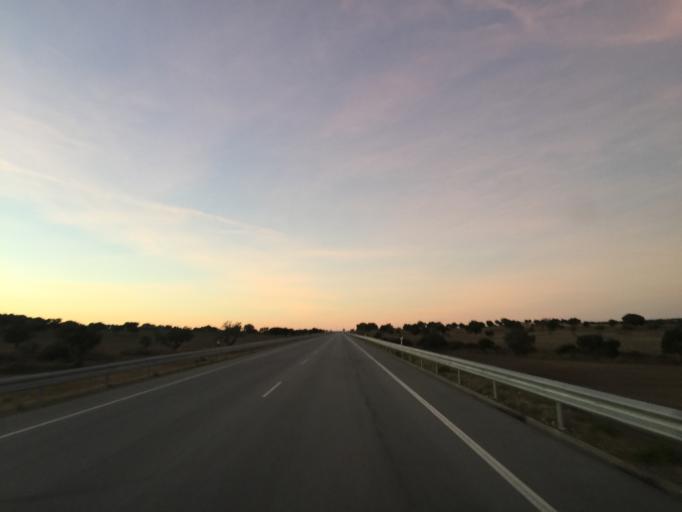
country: PT
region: Portalegre
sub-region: Alter do Chao
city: Alter do Chao
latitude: 39.2989
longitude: -7.6331
